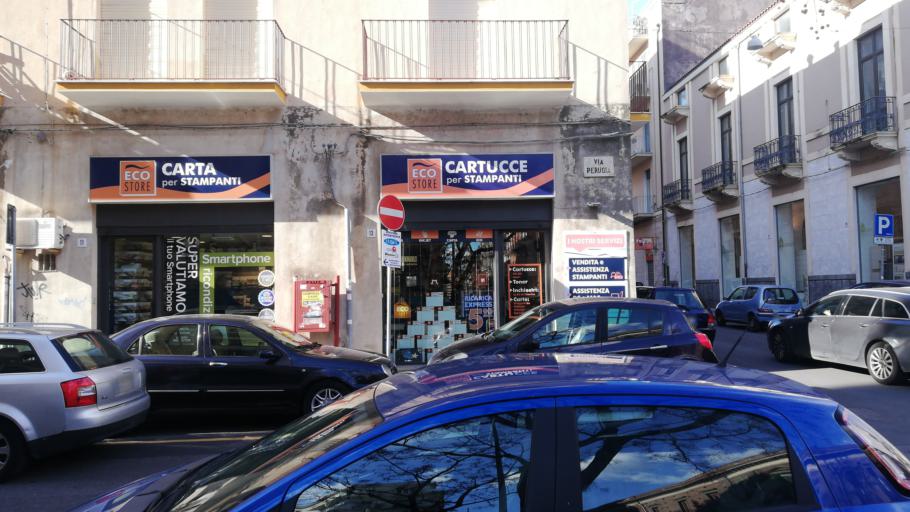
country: IT
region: Sicily
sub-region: Catania
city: Canalicchio
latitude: 37.5164
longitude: 15.0951
